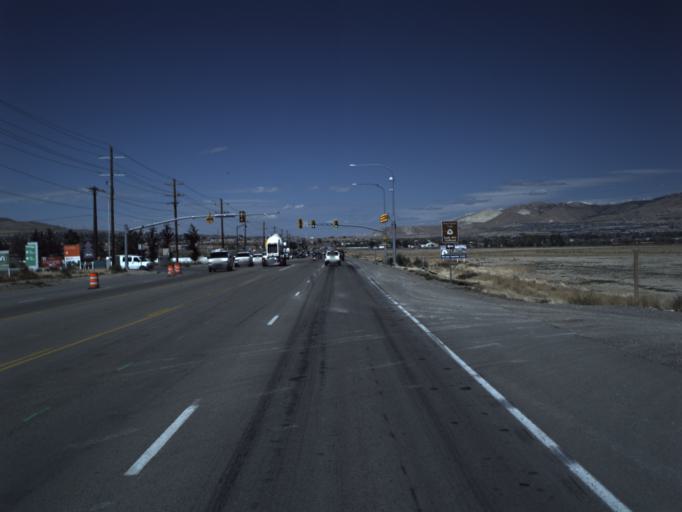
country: US
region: Utah
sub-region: Utah County
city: Saratoga Springs
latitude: 40.3606
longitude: -111.9162
